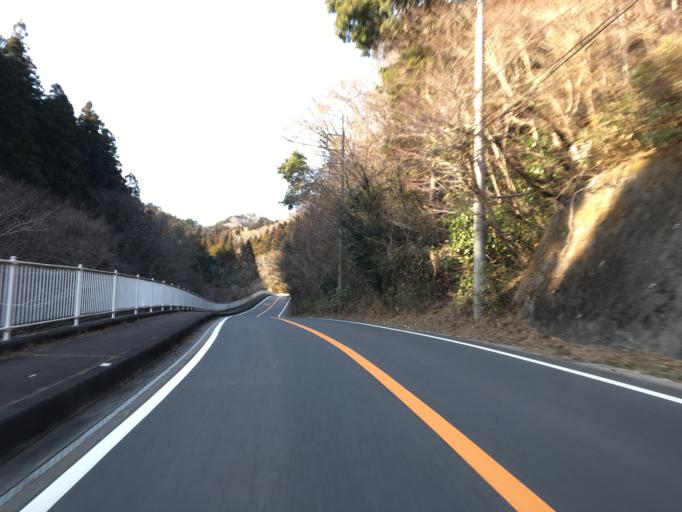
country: JP
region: Ibaraki
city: Takahagi
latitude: 36.7264
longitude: 140.6343
